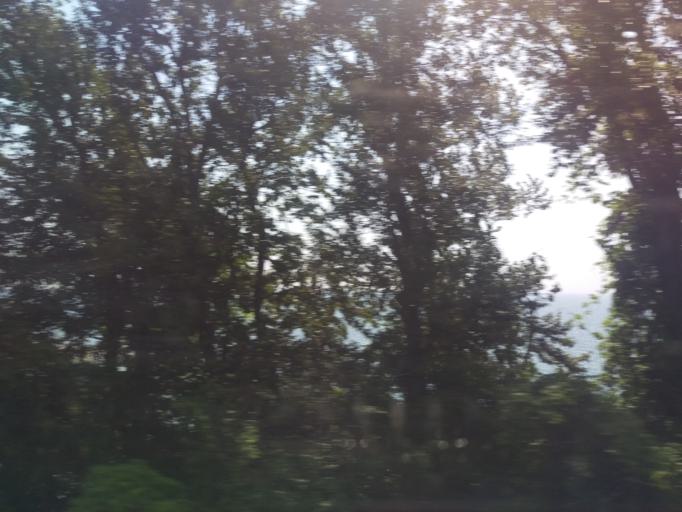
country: CA
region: Ontario
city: Scarborough
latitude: 43.7692
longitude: -79.1419
